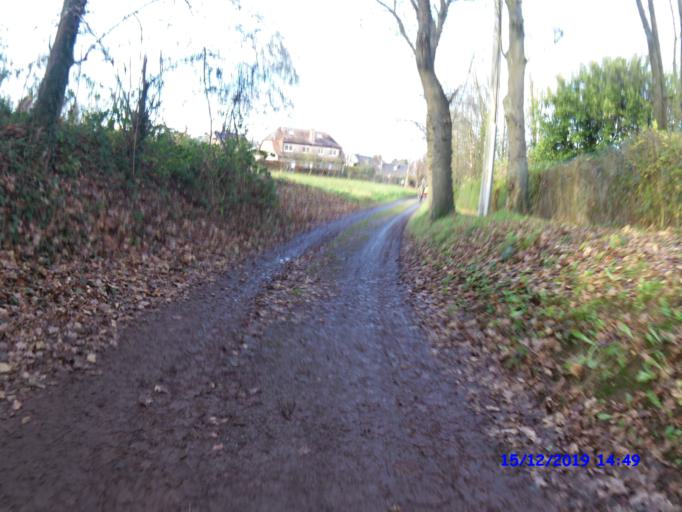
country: BE
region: Flanders
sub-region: Provincie Vlaams-Brabant
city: Beersel
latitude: 50.7582
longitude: 4.3156
